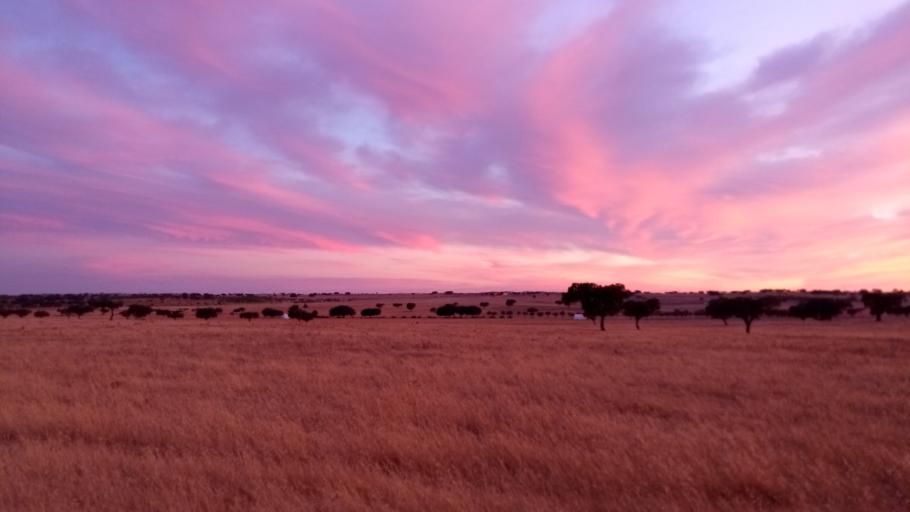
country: PT
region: Evora
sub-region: Reguengos de Monsaraz
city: Reguengos de Monsaraz
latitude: 38.3582
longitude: -7.4669
